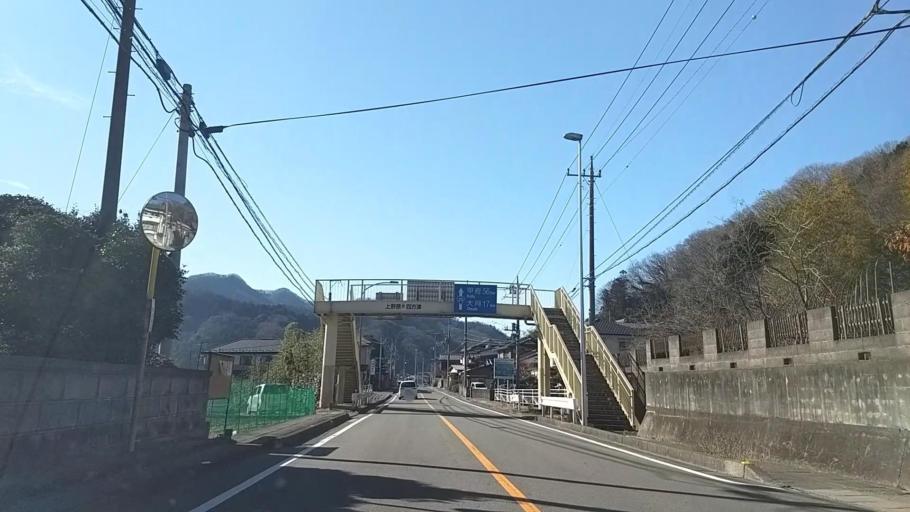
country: JP
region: Yamanashi
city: Uenohara
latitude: 35.6152
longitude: 139.0889
